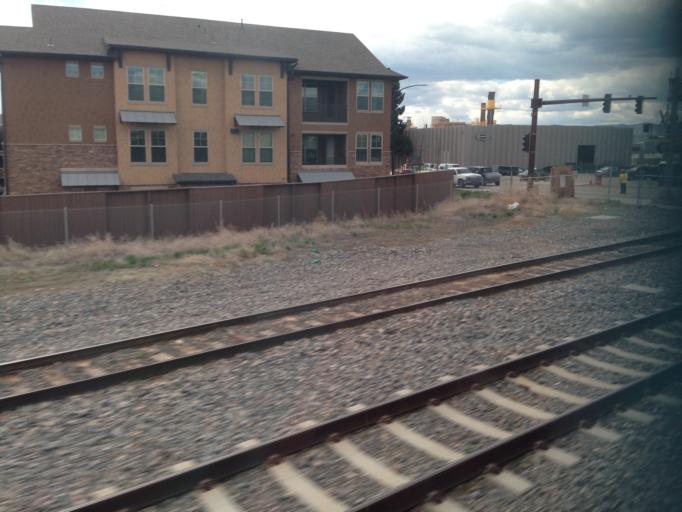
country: US
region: Colorado
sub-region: Jefferson County
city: Arvada
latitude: 39.7920
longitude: -105.1141
